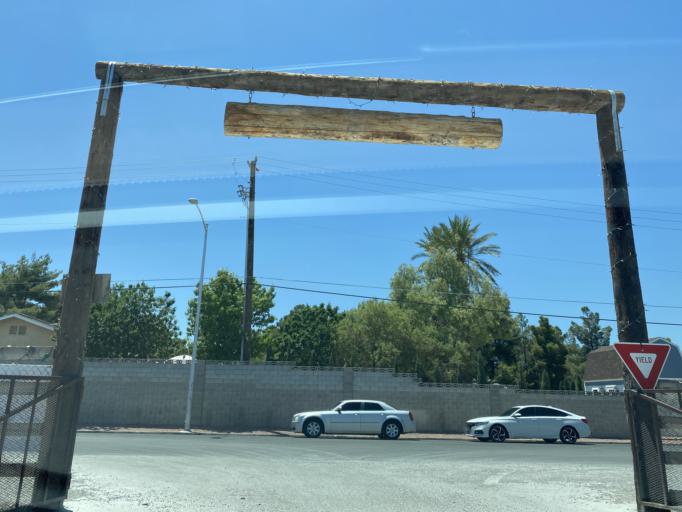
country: US
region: Nevada
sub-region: Clark County
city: Las Vegas
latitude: 36.2274
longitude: -115.2121
